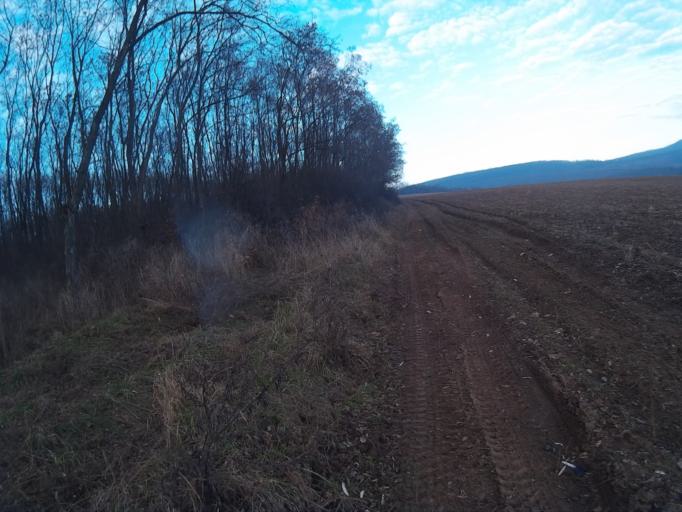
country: HU
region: Nograd
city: Rimoc
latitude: 47.9916
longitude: 19.4293
